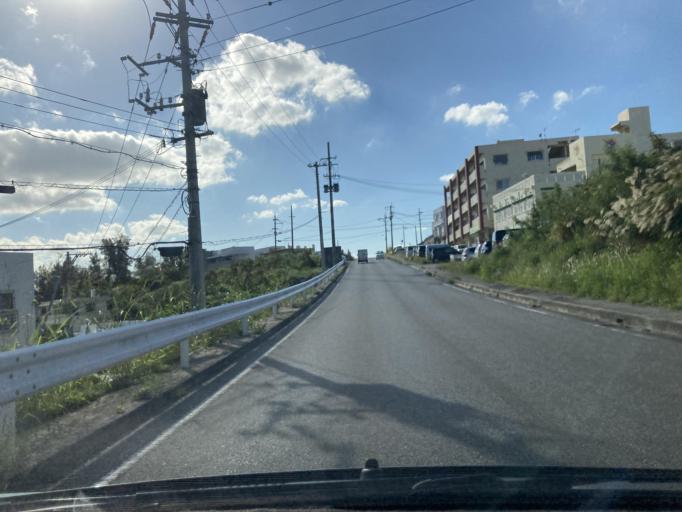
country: JP
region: Okinawa
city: Okinawa
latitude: 26.3392
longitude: 127.8289
